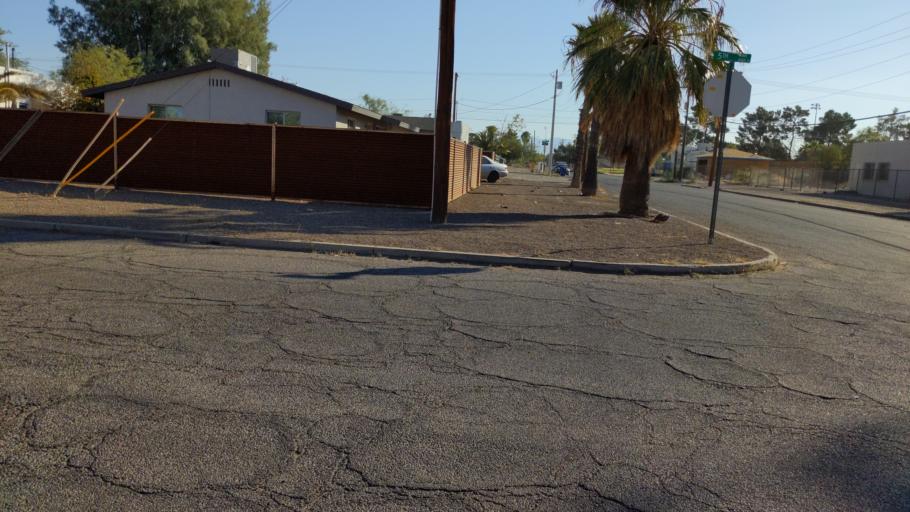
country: US
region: Arizona
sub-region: Pima County
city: South Tucson
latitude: 32.2083
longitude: -110.9670
